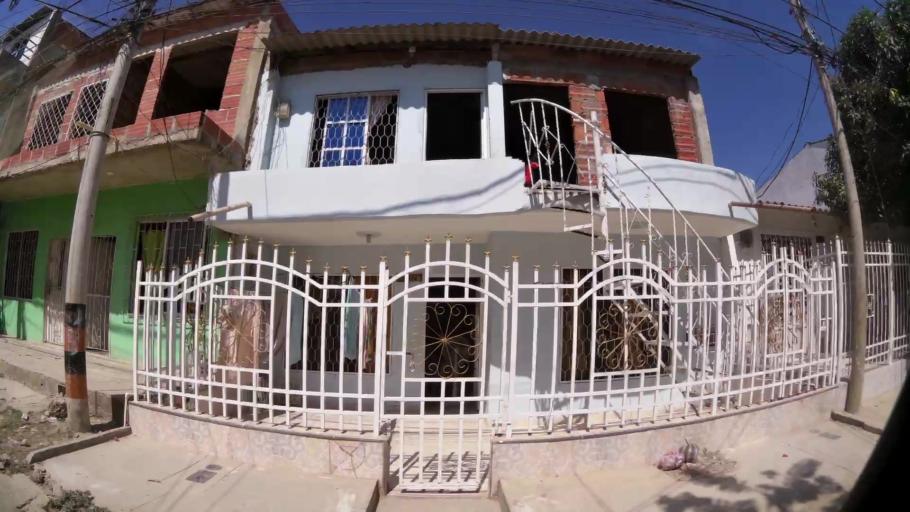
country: CO
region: Bolivar
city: Cartagena
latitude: 10.3845
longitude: -75.4558
